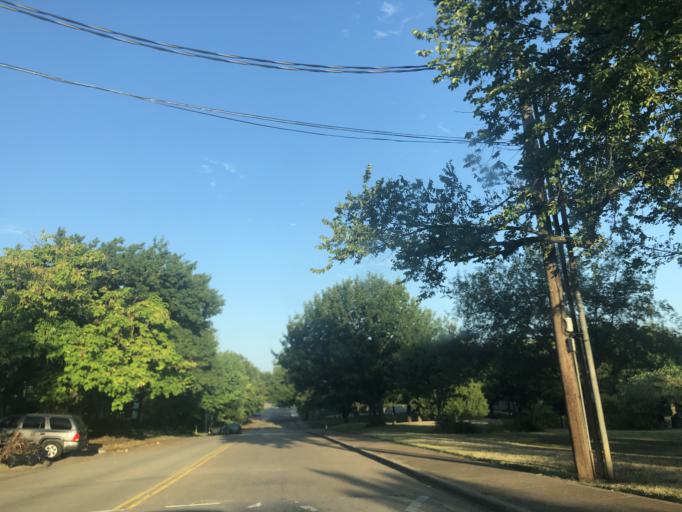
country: US
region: Texas
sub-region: Dallas County
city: Dallas
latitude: 32.7524
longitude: -96.8338
